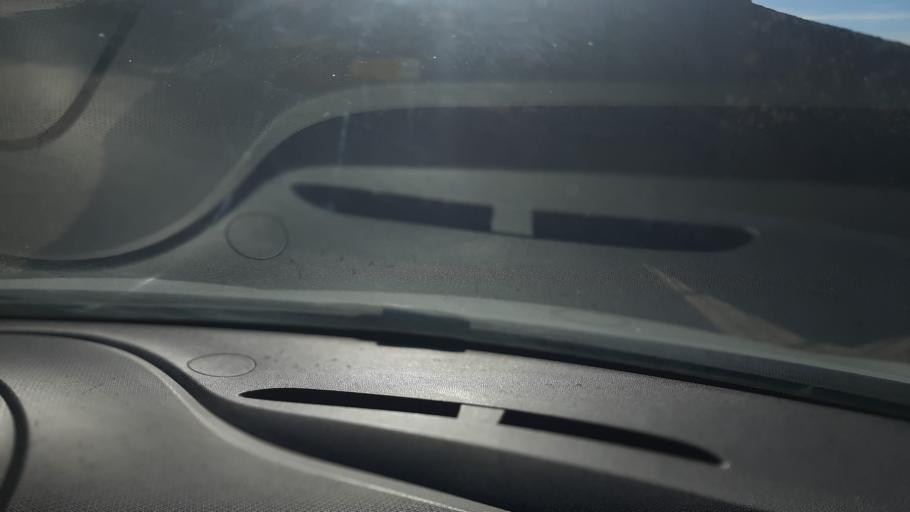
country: ES
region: Castille and Leon
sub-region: Provincia de Salamanca
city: Guijo de Avila
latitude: 40.5297
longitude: -5.6405
